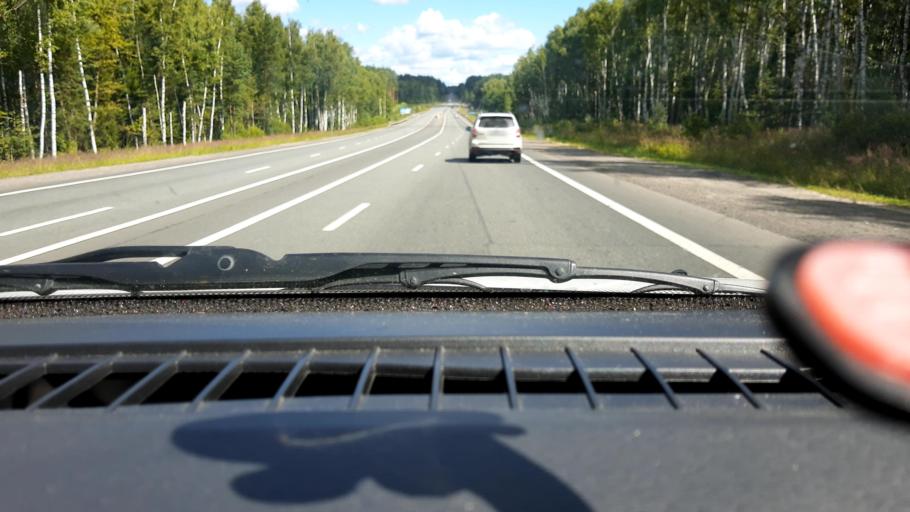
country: RU
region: Nizjnij Novgorod
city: Arzamas
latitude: 55.4946
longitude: 43.8910
